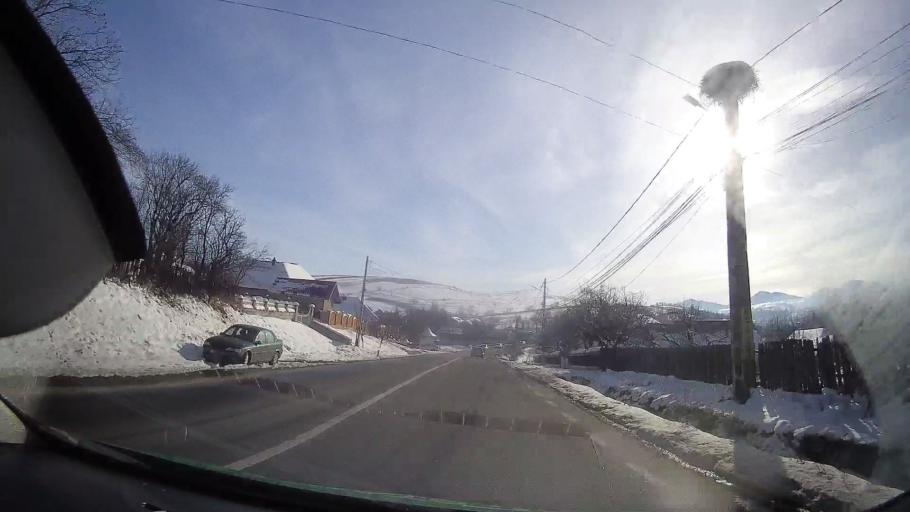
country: RO
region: Neamt
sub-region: Comuna Baltatesti
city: Valea Seaca
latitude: 47.1324
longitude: 26.3150
